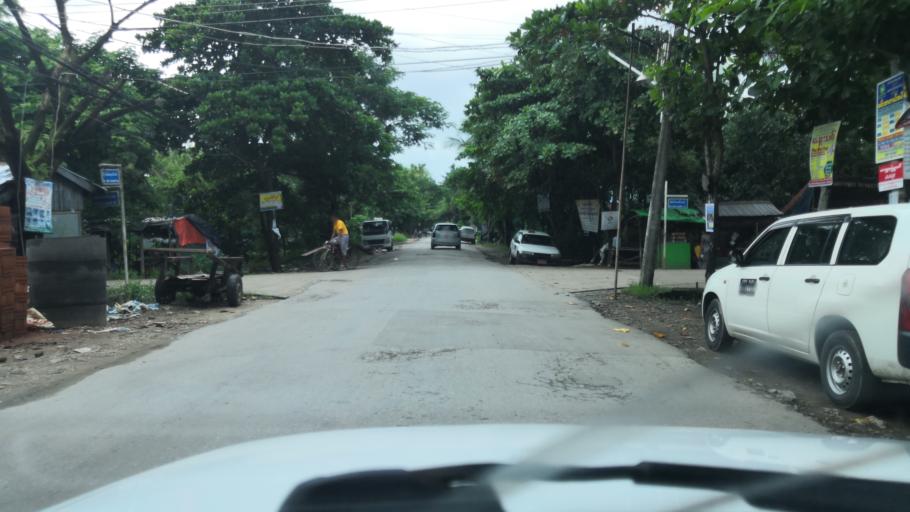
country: MM
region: Yangon
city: Yangon
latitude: 16.8785
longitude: 96.1810
